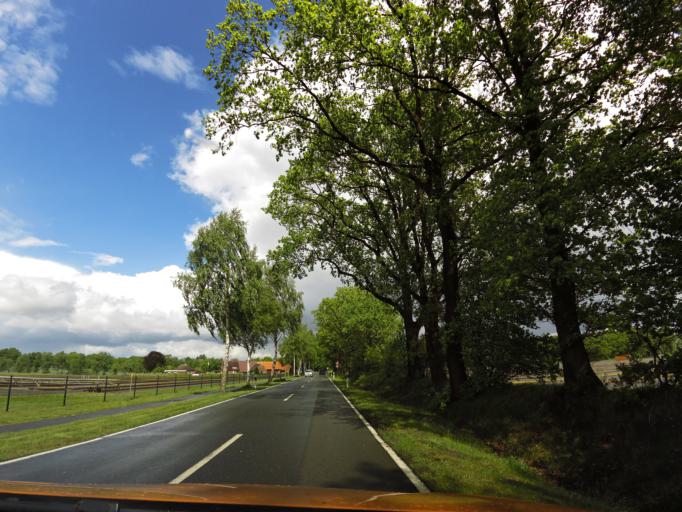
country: DE
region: Lower Saxony
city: Ganderkesee
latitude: 53.0117
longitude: 8.5414
